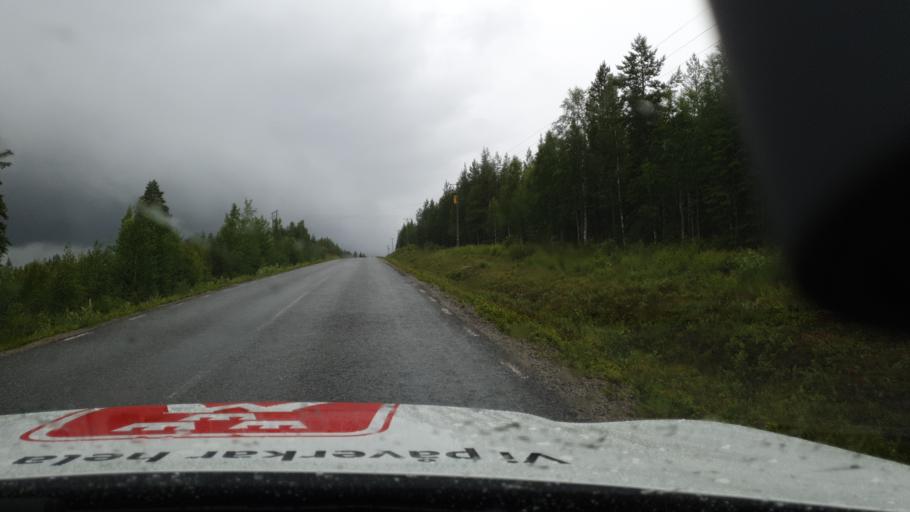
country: SE
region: Vaesterbotten
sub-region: Vindelns Kommun
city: Vindeln
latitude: 64.3975
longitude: 19.6670
